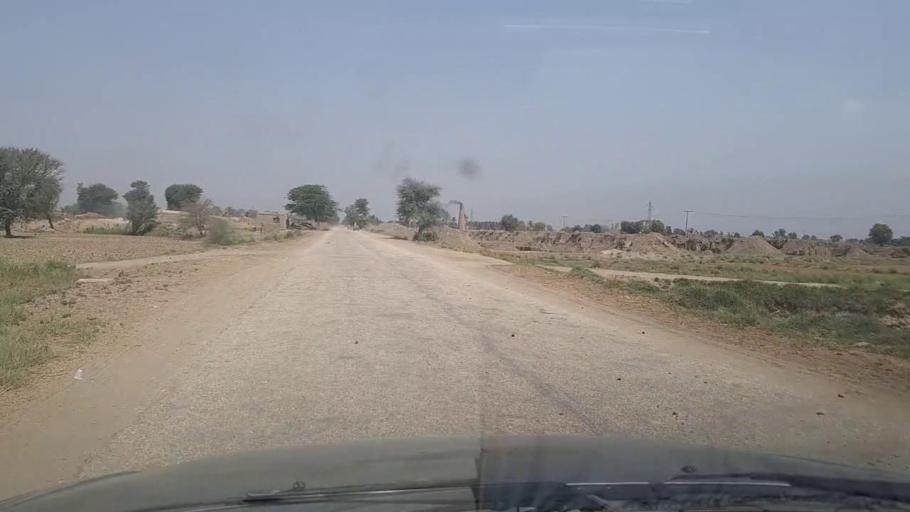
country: PK
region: Sindh
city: Setharja Old
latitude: 27.1467
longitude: 68.5250
